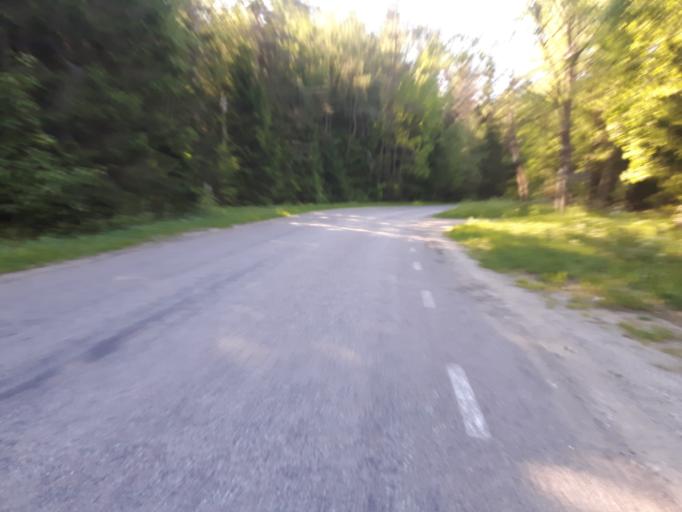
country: EE
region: Harju
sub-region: Loksa linn
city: Loksa
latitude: 59.5669
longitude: 25.9725
